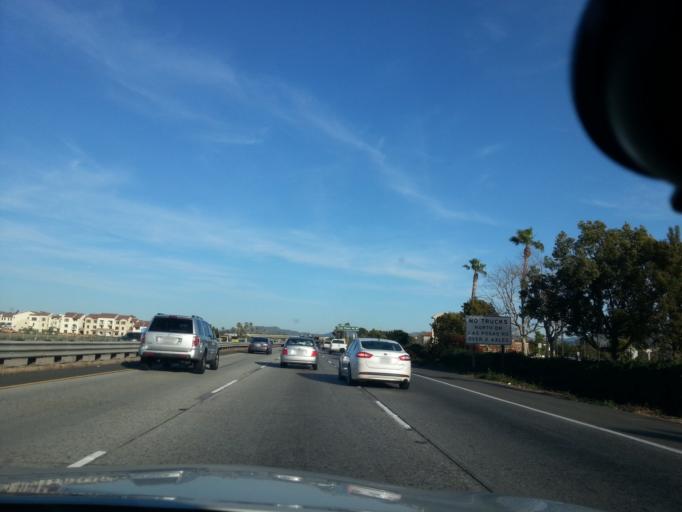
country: US
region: California
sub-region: Ventura County
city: Camarillo
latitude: 34.2196
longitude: -119.0769
